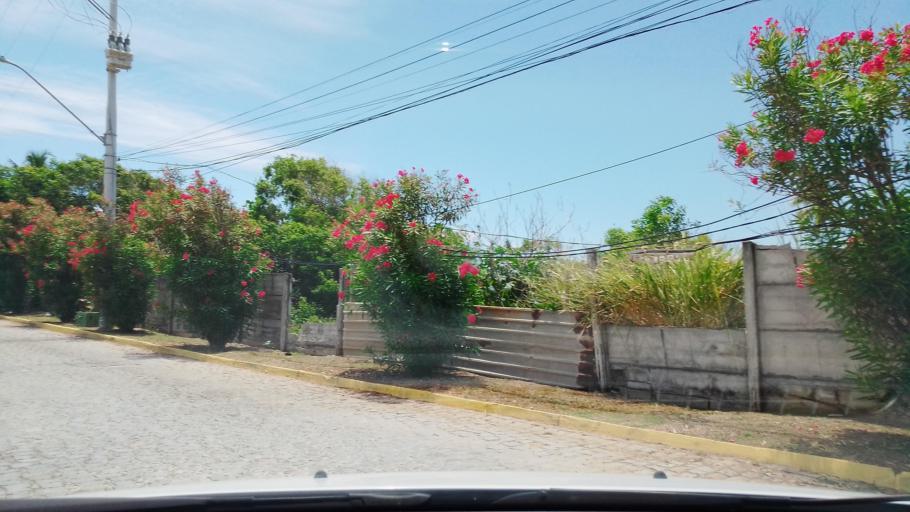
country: BR
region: Bahia
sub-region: Lauro De Freitas
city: Lauro de Freitas
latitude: -12.9364
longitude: -38.3287
